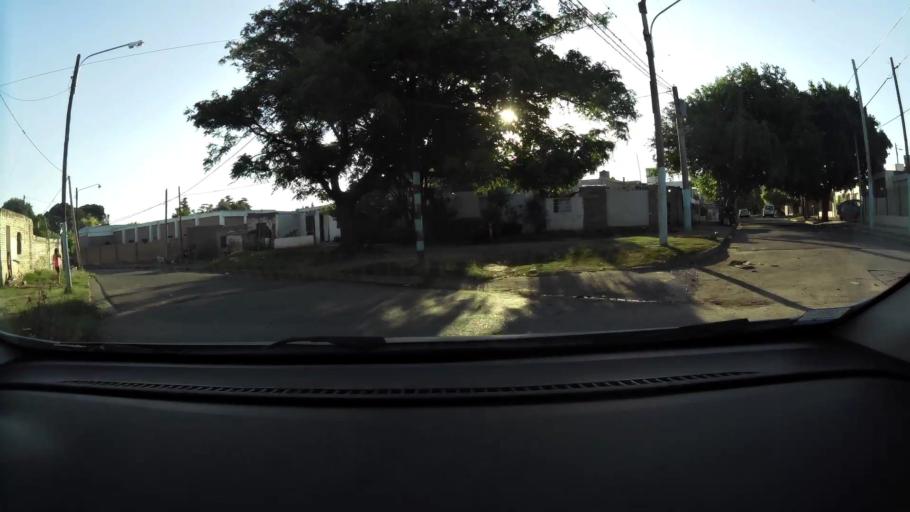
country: AR
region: Cordoba
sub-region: Departamento de Capital
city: Cordoba
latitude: -31.3733
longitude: -64.2030
